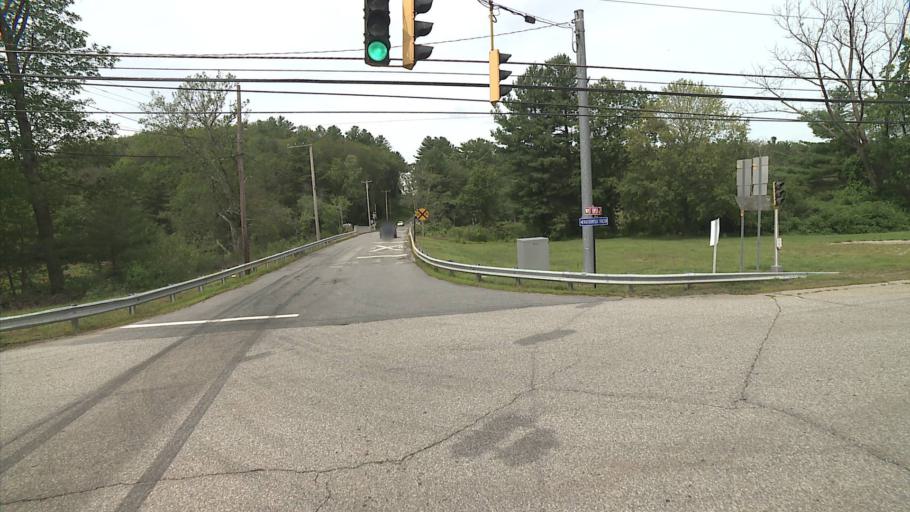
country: US
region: Connecticut
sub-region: Windham County
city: Thompson
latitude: 41.9475
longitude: -71.8882
